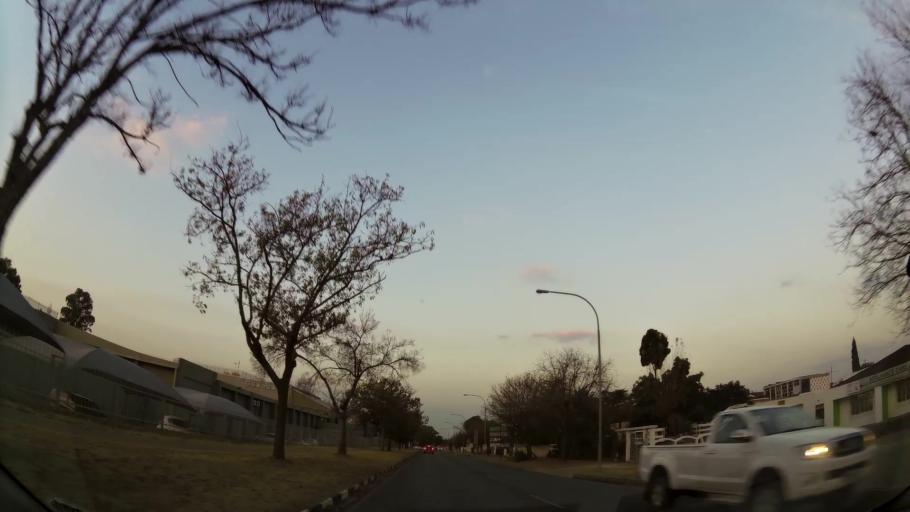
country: ZA
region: Gauteng
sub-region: Ekurhuleni Metropolitan Municipality
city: Benoni
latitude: -26.1638
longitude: 28.3215
